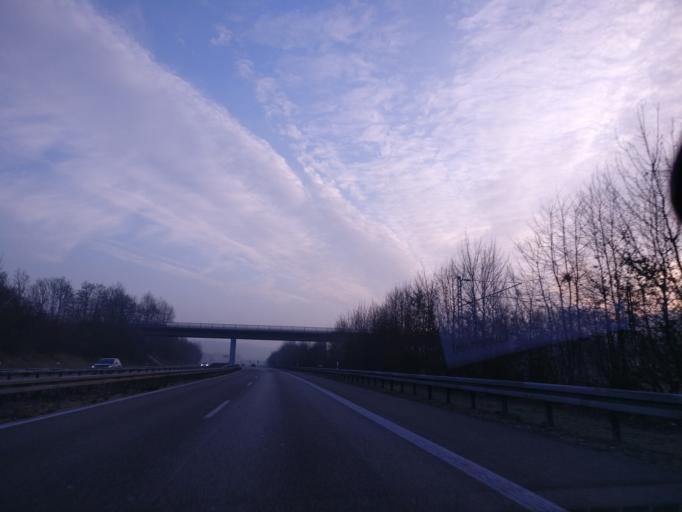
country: DE
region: Baden-Wuerttemberg
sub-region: Regierungsbezirk Stuttgart
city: Lorch
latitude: 48.7930
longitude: 9.6499
